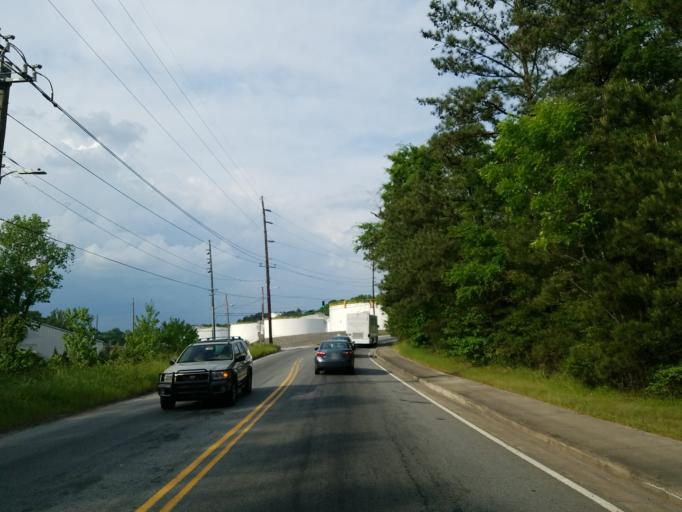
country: US
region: Georgia
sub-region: Cobb County
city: Vinings
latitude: 33.8013
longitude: -84.4873
